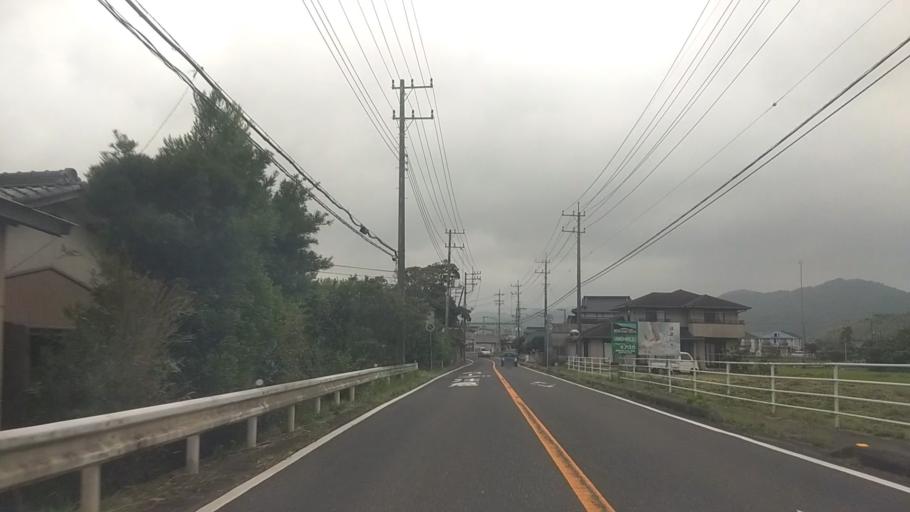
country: JP
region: Chiba
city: Kawaguchi
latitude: 35.1252
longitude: 140.0590
